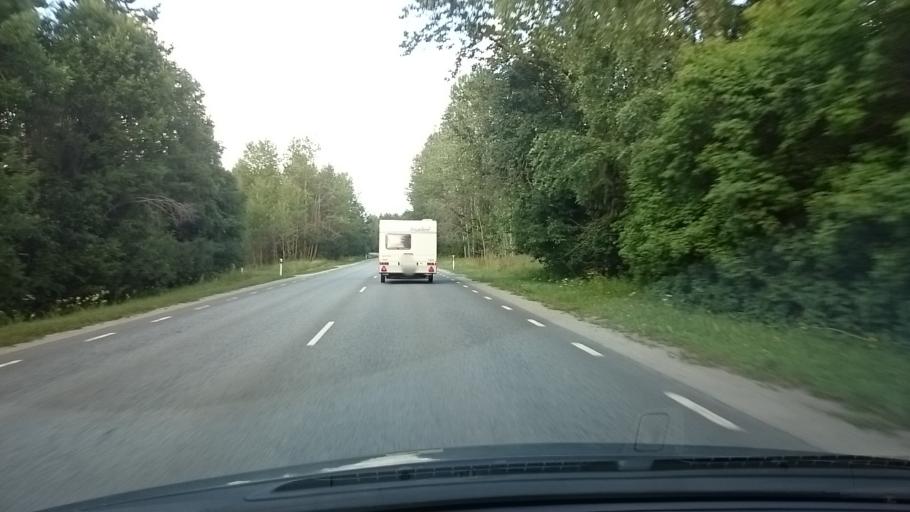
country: EE
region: Harju
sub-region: Keila linn
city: Keila
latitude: 59.2584
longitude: 24.2886
